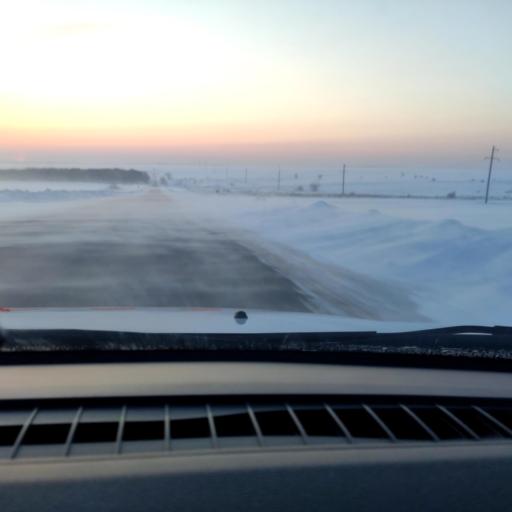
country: RU
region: Samara
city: Georgiyevka
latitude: 53.4175
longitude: 50.9165
